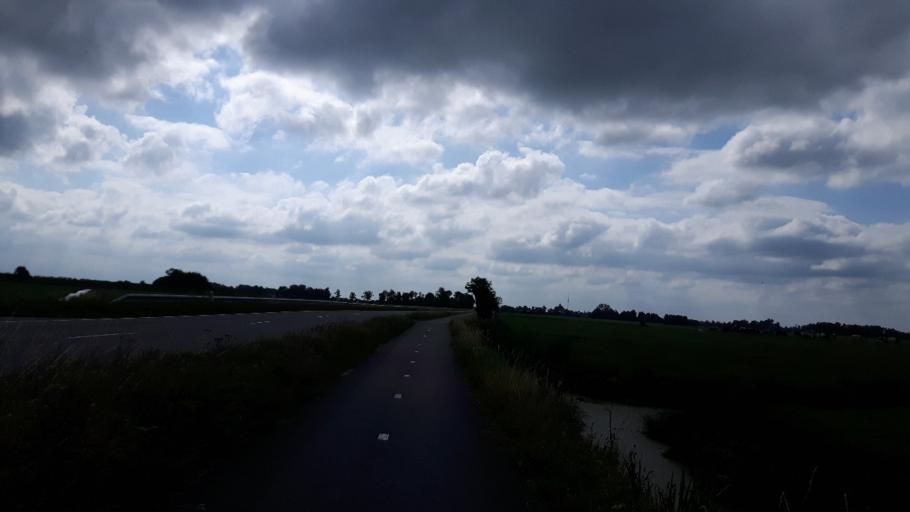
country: NL
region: Utrecht
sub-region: Gemeente Woerden
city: Woerden
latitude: 52.1345
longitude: 4.8609
